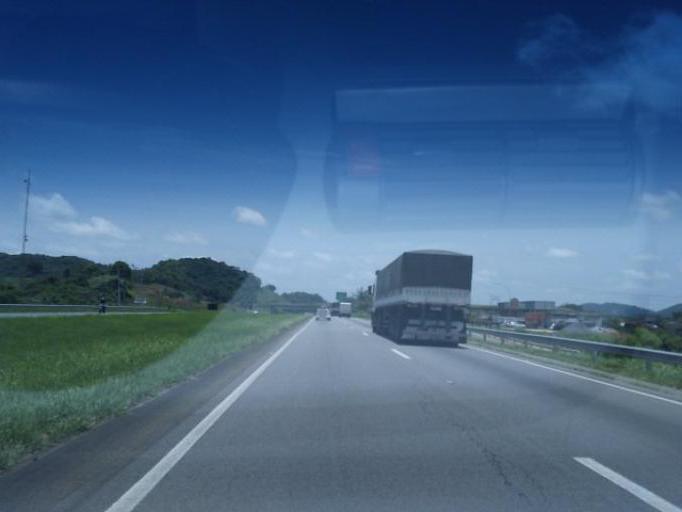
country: BR
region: Sao Paulo
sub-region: Juquia
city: Juquia
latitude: -24.3307
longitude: -47.6282
